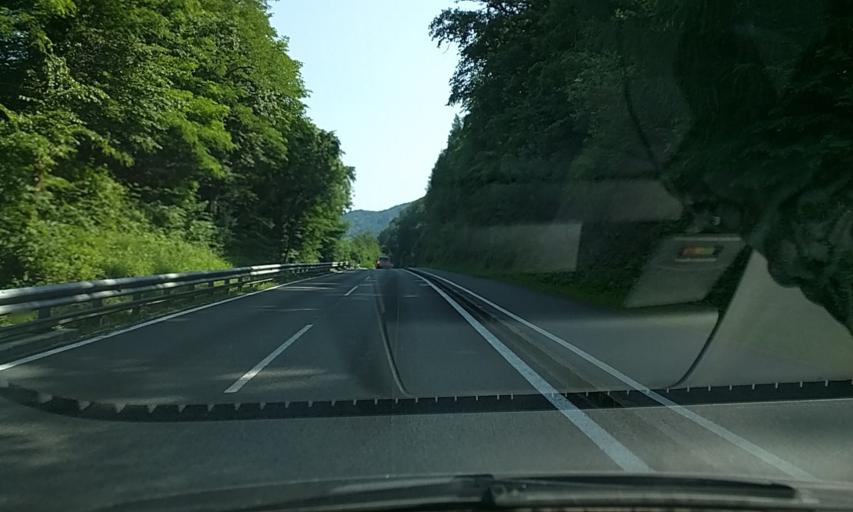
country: AT
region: Lower Austria
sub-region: Politischer Bezirk Krems
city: Aggsbach
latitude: 48.2690
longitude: 15.3837
